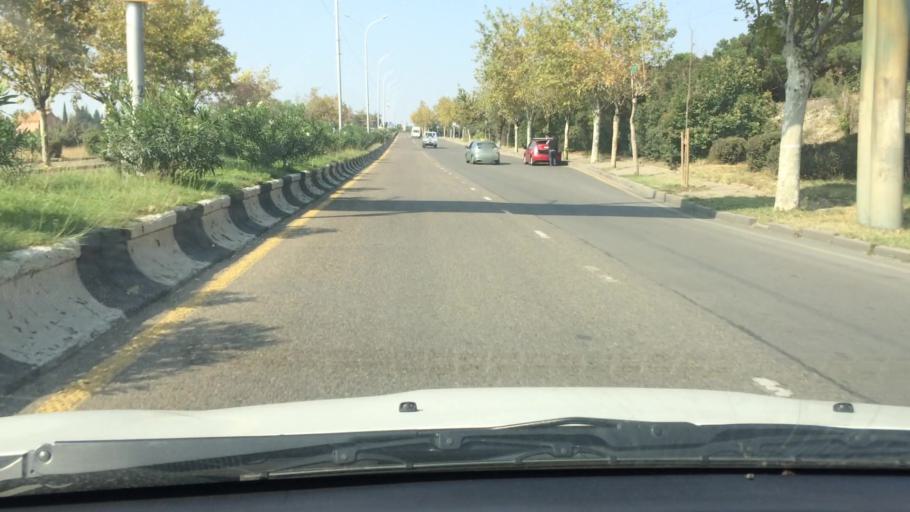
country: GE
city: Didi Lilo
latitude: 41.6814
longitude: 44.9567
